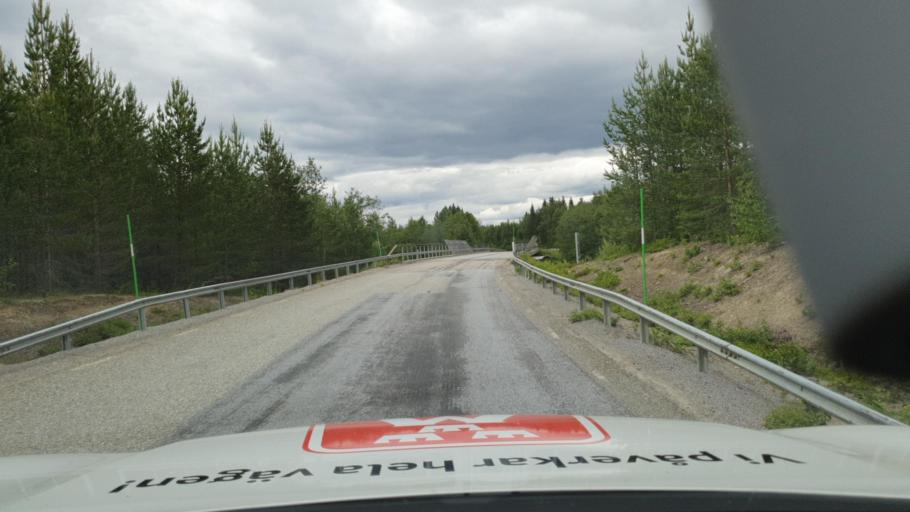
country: SE
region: Vaesterbotten
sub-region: Bjurholms Kommun
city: Bjurholm
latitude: 63.7708
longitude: 19.2453
